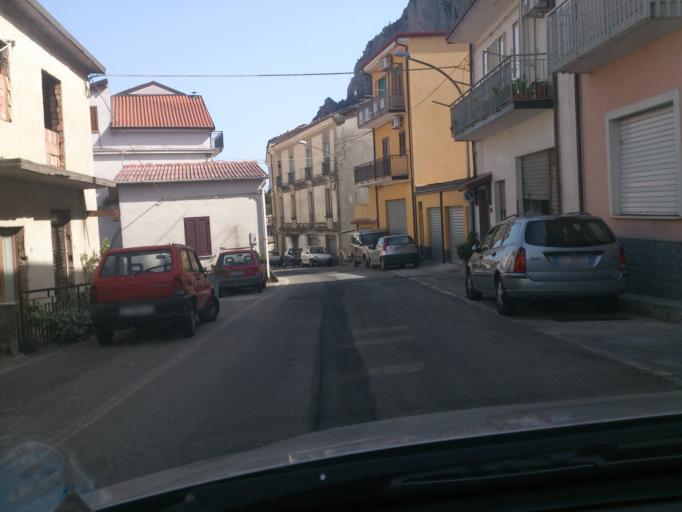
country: IT
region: Calabria
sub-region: Provincia di Reggio Calabria
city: Pazzano
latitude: 38.4767
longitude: 16.4505
